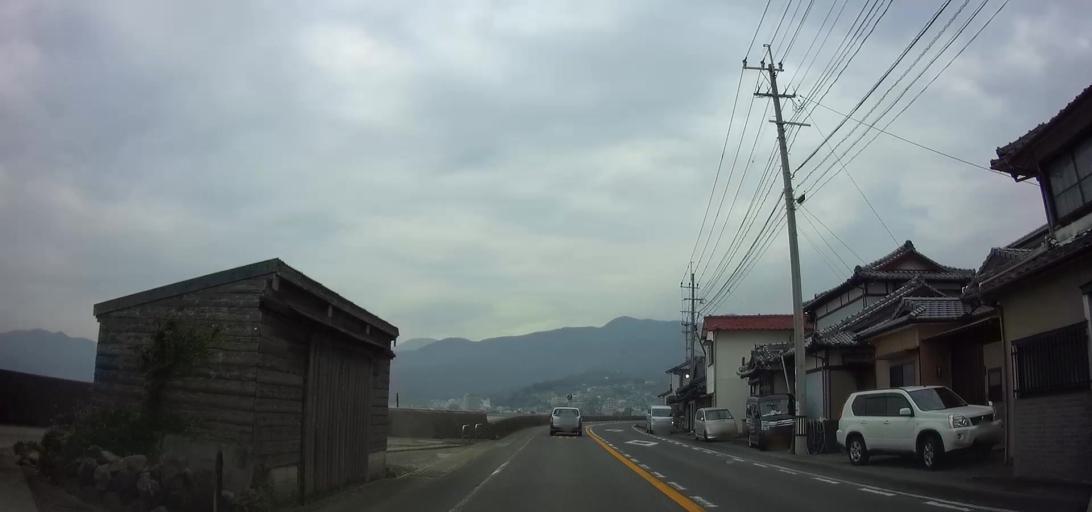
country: JP
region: Nagasaki
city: Shimabara
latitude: 32.7161
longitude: 130.1921
